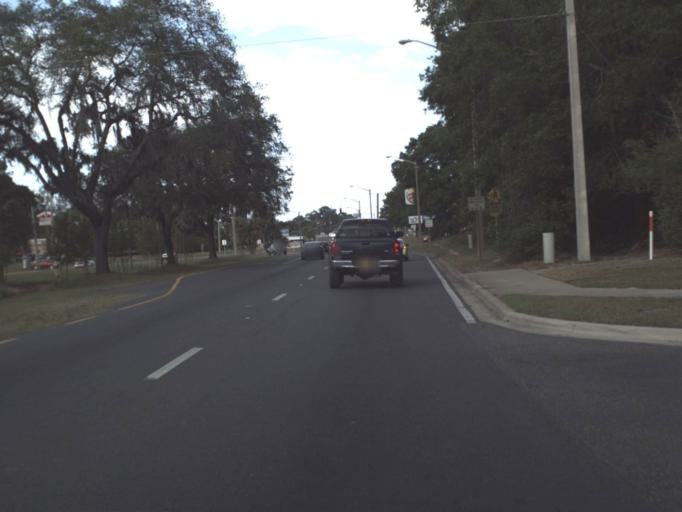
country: US
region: Florida
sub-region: Marion County
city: Ocala
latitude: 29.2098
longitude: -82.0671
